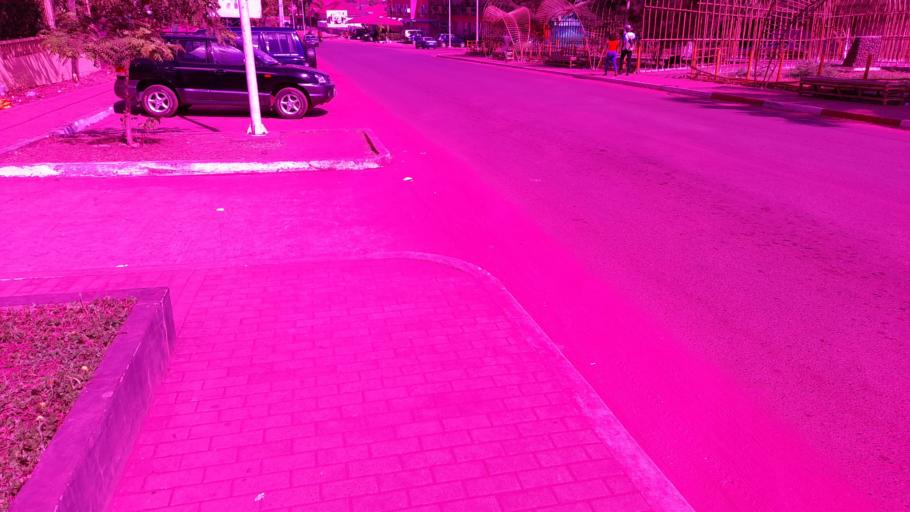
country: GW
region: Bissau
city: Bissau
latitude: 11.8592
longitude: -15.5899
